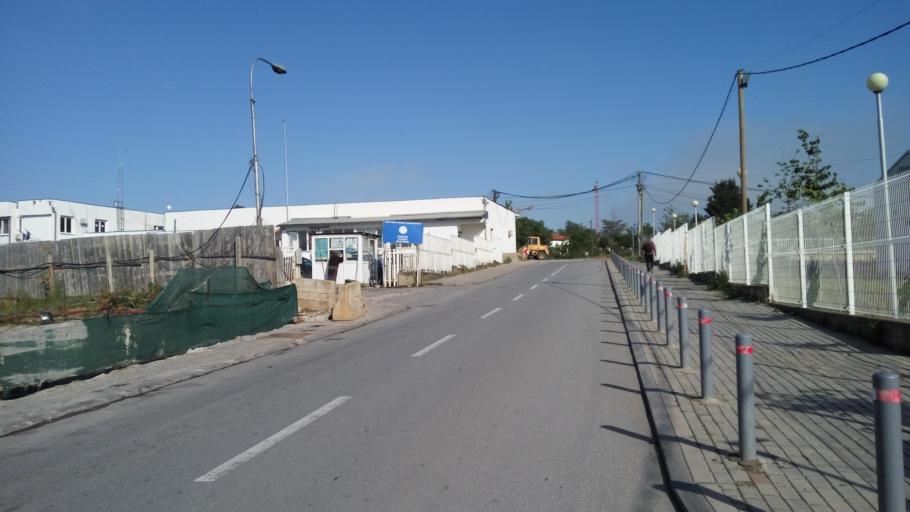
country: XK
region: Pristina
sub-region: Komuna e Prishtines
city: Pristina
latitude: 42.6539
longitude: 21.1472
